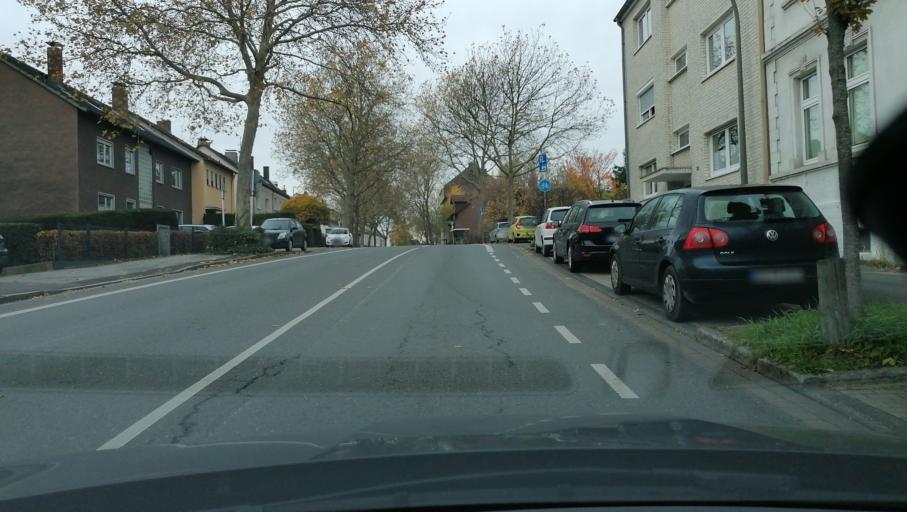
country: DE
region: North Rhine-Westphalia
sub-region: Regierungsbezirk Arnsberg
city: Dortmund
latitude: 51.4938
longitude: 7.5184
